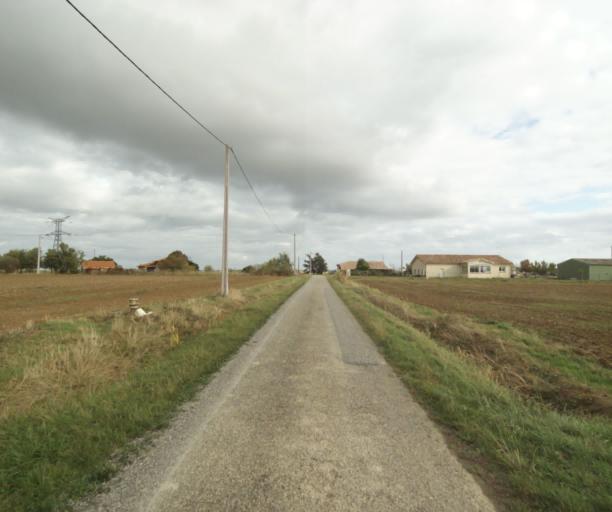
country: FR
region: Midi-Pyrenees
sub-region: Departement du Tarn-et-Garonne
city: Finhan
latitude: 43.9030
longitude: 1.1072
